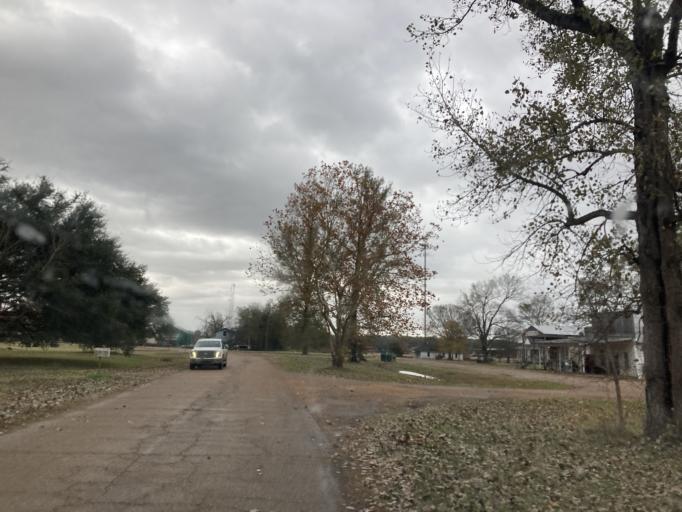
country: US
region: Mississippi
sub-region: Yazoo County
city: Yazoo City
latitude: 32.9897
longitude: -90.4480
